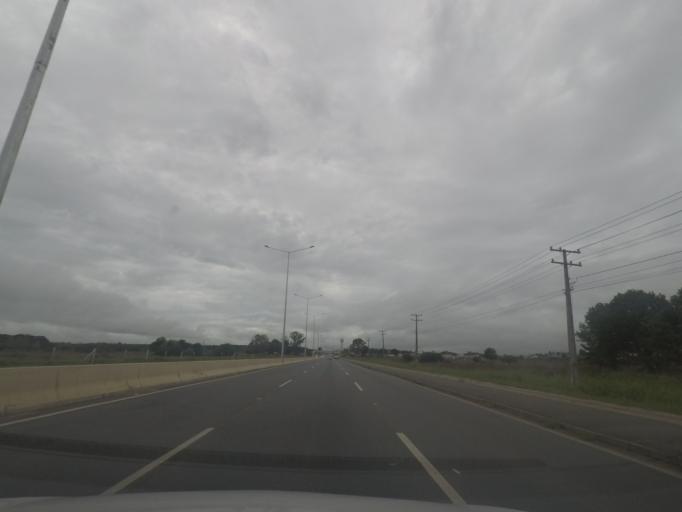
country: BR
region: Parana
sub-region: Pinhais
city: Pinhais
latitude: -25.4476
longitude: -49.1335
